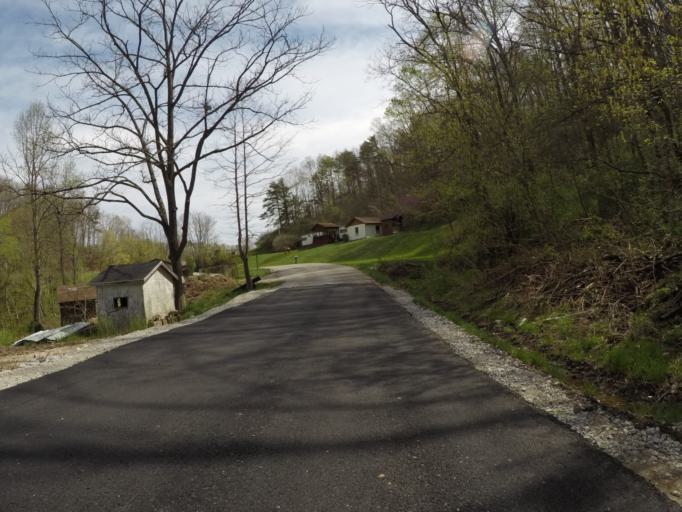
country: US
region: West Virginia
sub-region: Cabell County
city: Pea Ridge
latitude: 38.3435
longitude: -82.3601
